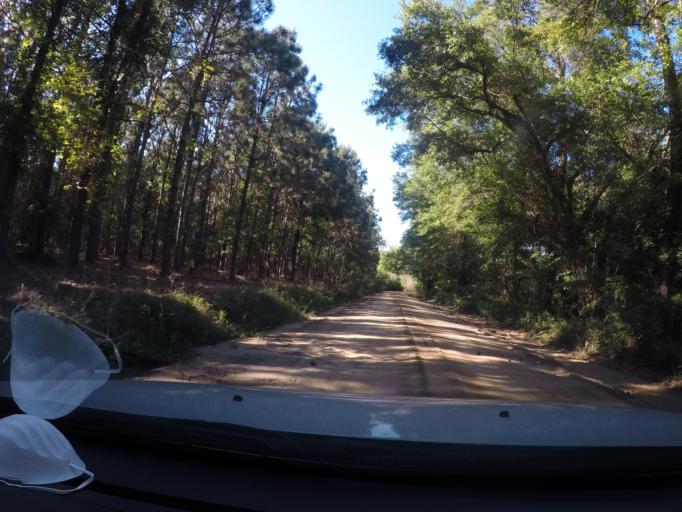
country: US
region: Georgia
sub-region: Bulloch County
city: Brooklet
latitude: 32.3274
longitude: -81.7416
